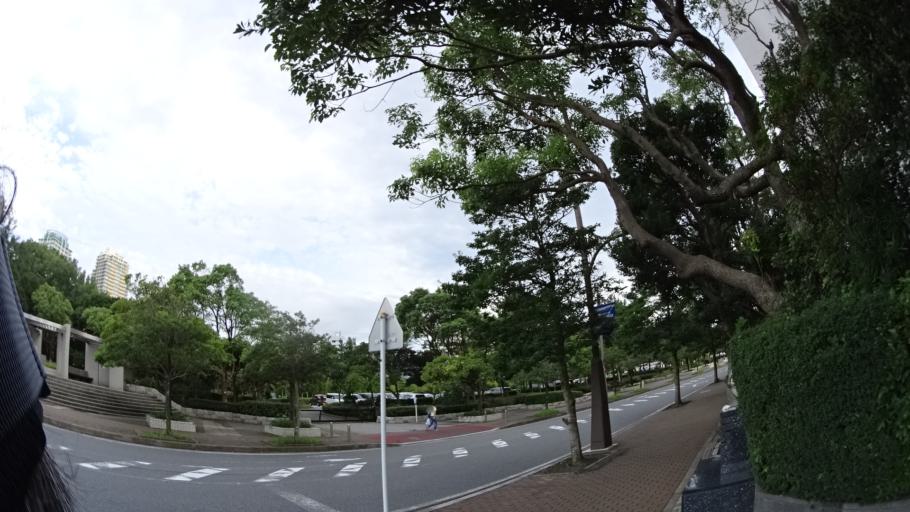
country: JP
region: Chiba
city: Funabashi
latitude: 35.6454
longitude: 140.0415
